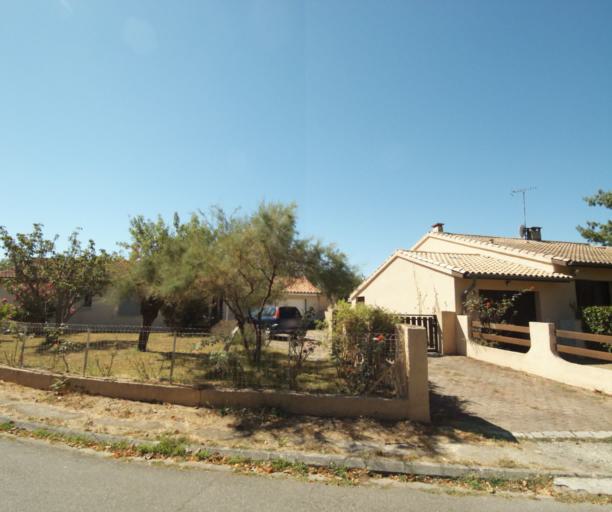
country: FR
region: Midi-Pyrenees
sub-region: Departement de la Haute-Garonne
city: Pechabou
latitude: 43.5078
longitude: 1.5162
